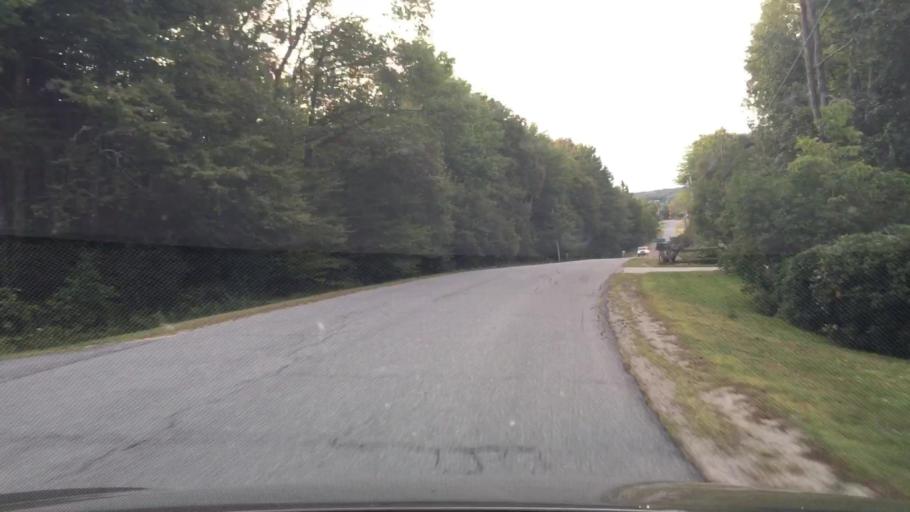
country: US
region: Maine
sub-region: Waldo County
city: Stockton Springs
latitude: 44.4922
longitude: -68.8692
